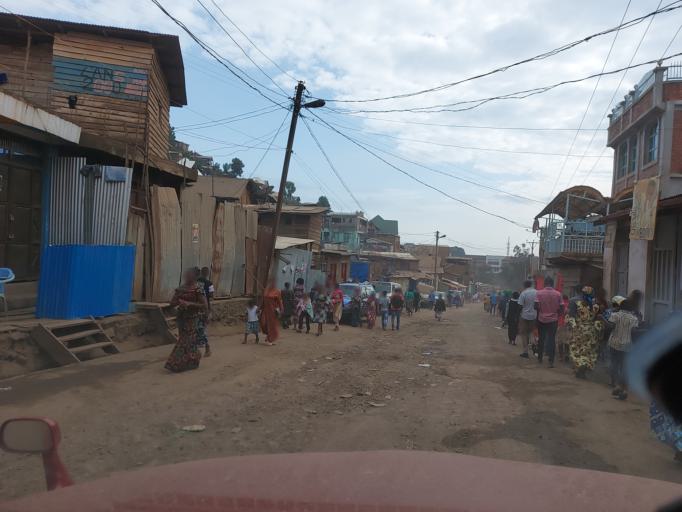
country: CD
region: South Kivu
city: Bukavu
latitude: -2.5101
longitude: 28.8477
